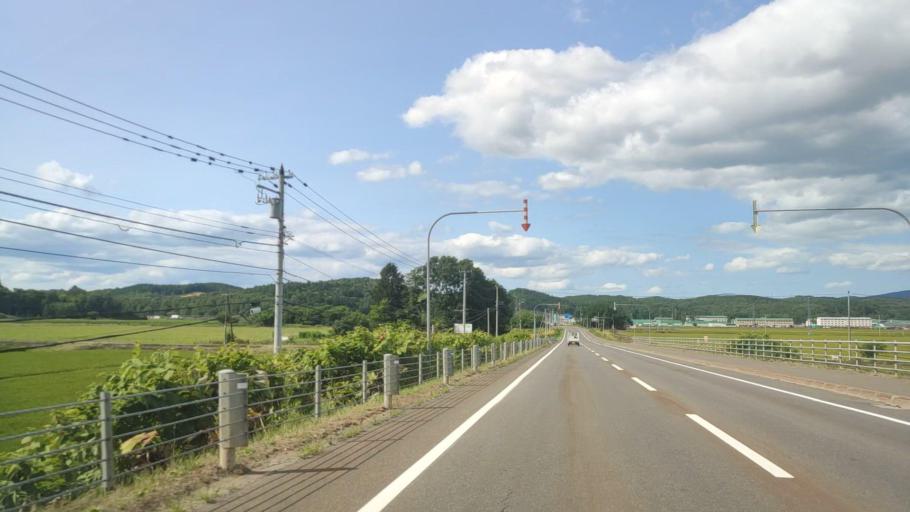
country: JP
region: Hokkaido
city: Nayoro
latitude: 44.3730
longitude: 142.4361
